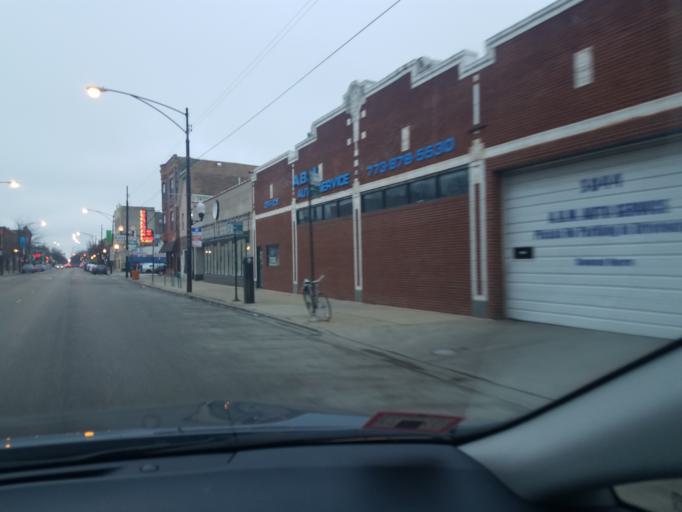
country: US
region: Illinois
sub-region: Cook County
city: Lincolnwood
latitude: 41.9612
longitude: -87.7050
